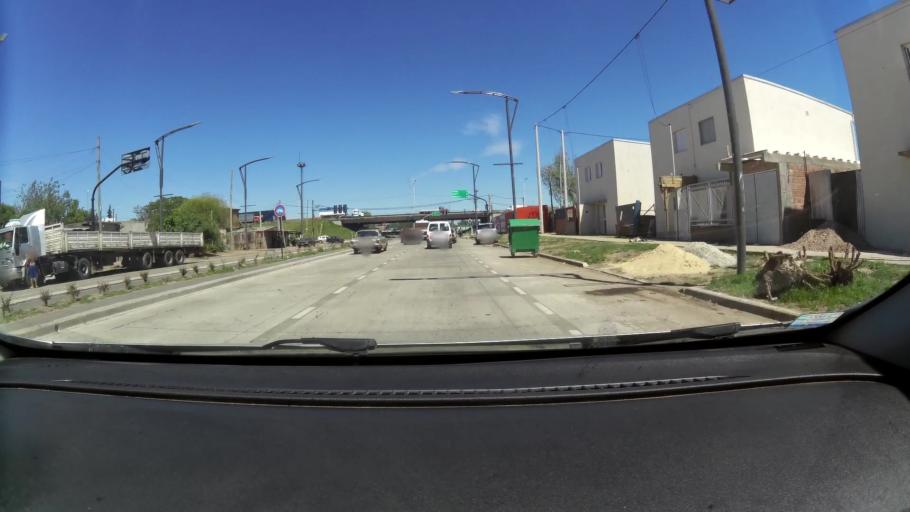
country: AR
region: Santa Fe
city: Perez
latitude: -32.9595
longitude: -60.7191
